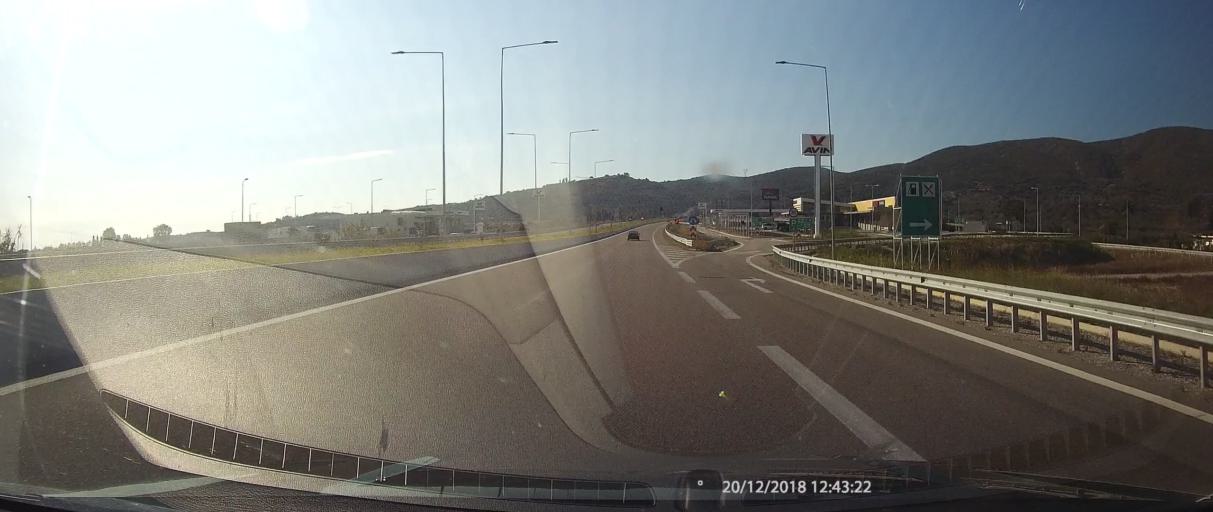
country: GR
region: West Greece
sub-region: Nomos Aitolias kai Akarnanias
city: Galatas
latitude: 38.3881
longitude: 21.5461
